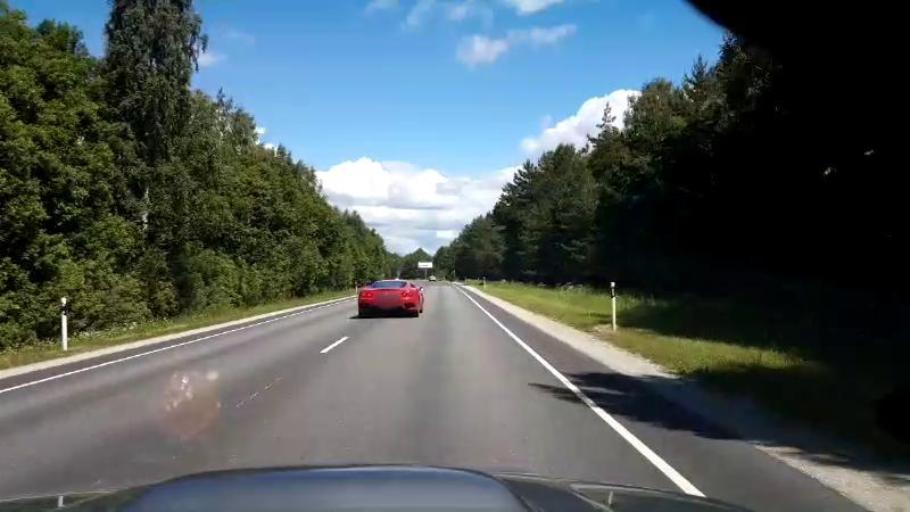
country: EE
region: Paernumaa
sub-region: Paernu linn
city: Parnu
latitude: 58.2307
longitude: 24.5021
